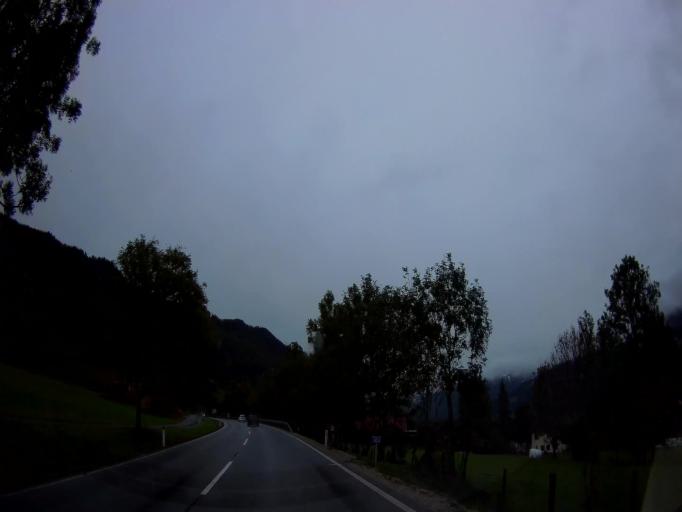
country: AT
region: Styria
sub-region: Politischer Bezirk Liezen
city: Pruggern
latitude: 47.4235
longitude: 13.8649
